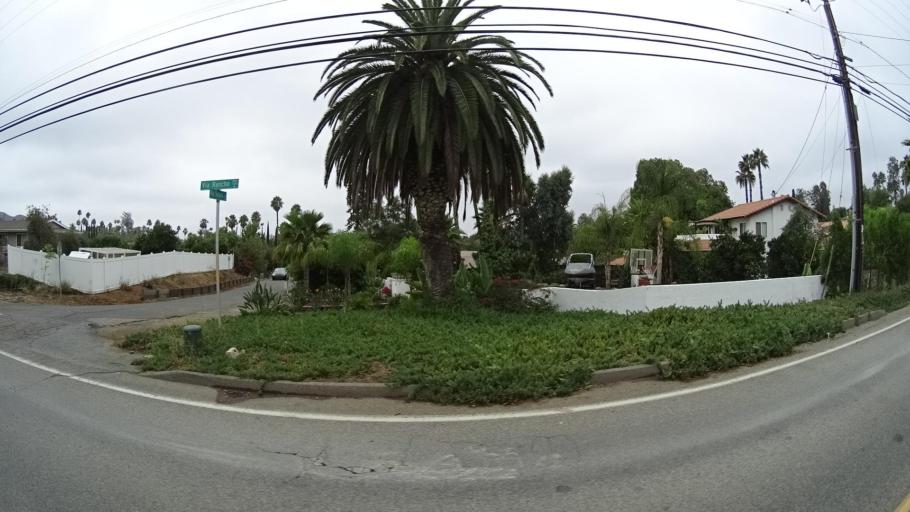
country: US
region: California
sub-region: San Diego County
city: Escondido
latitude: 33.0778
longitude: -117.0979
